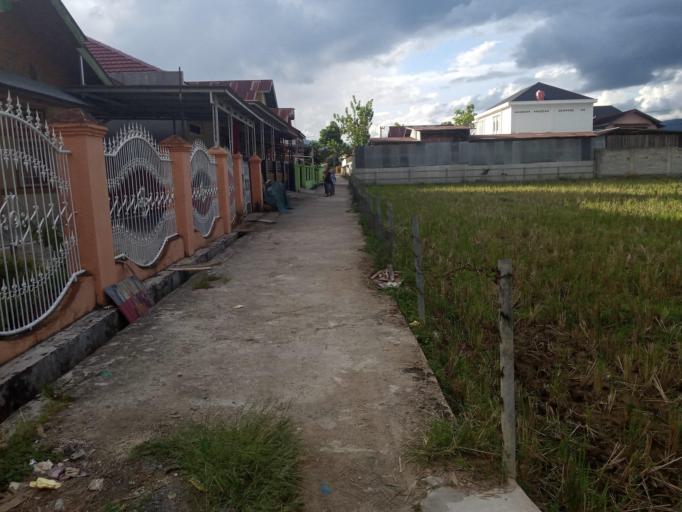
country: ID
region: Jambi
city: Semurup
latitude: -1.9883
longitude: 101.3667
